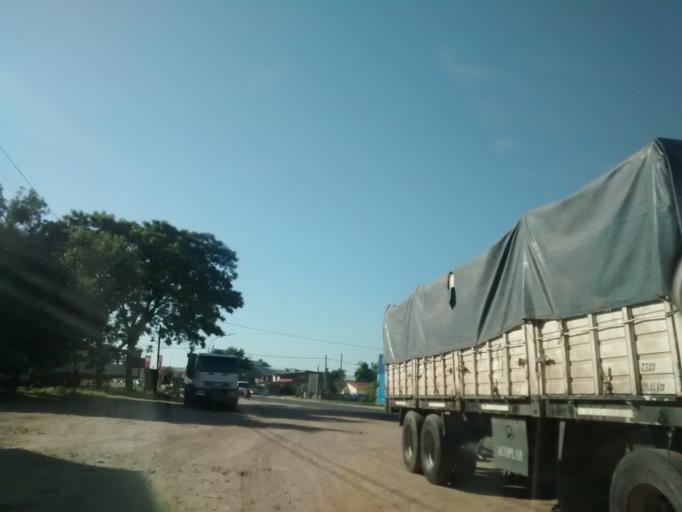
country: AR
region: Chaco
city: Fontana
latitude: -27.4322
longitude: -59.0092
